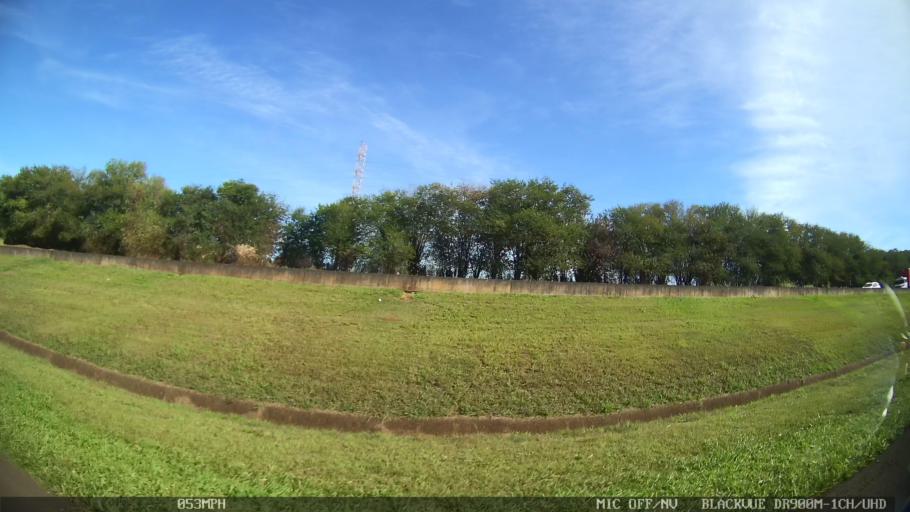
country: BR
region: Sao Paulo
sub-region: Leme
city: Leme
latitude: -22.2683
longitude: -47.3913
